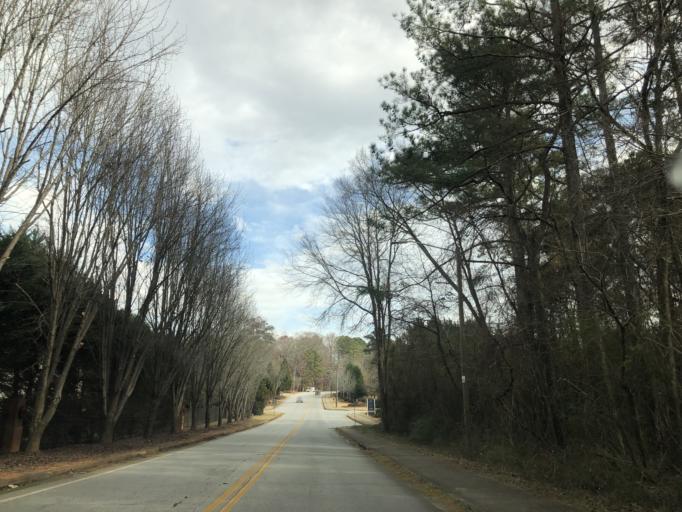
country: US
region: Georgia
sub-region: DeKalb County
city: Panthersville
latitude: 33.6655
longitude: -84.2090
